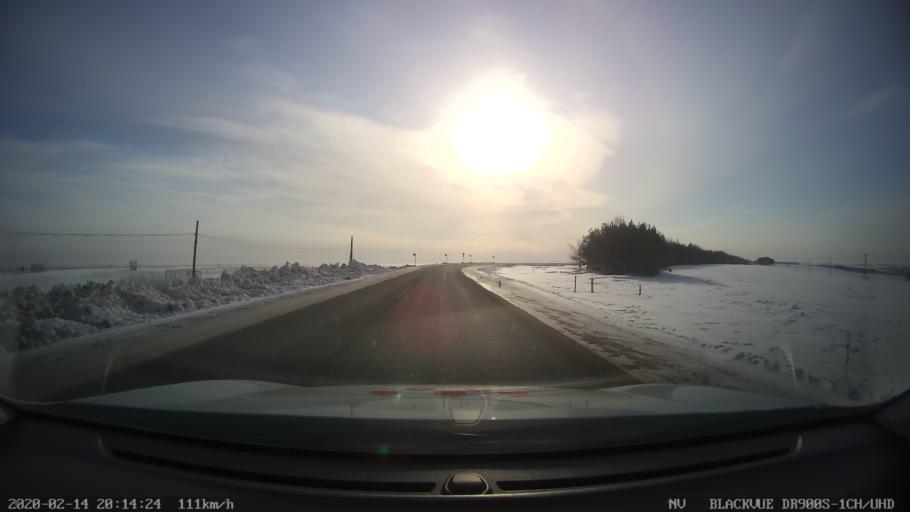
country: RU
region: Tatarstan
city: Verkhniy Uslon
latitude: 55.6454
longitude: 48.8752
